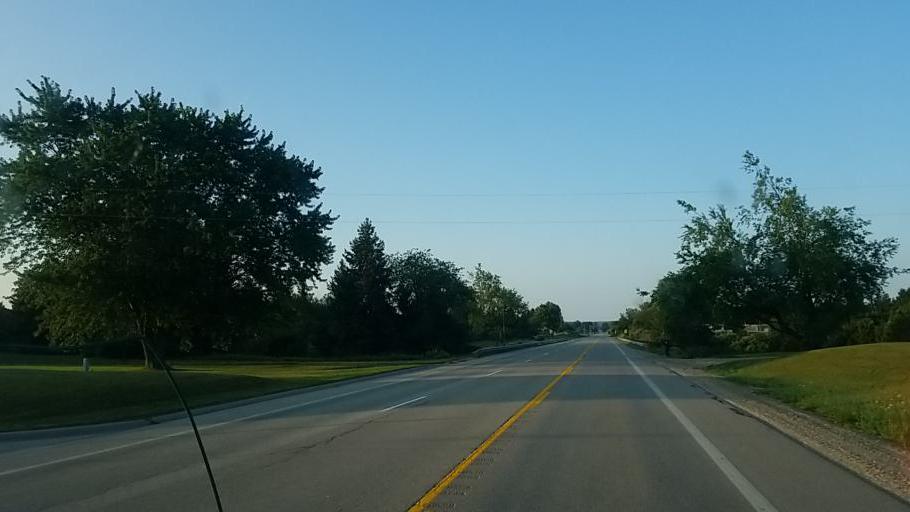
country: US
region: Michigan
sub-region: Isabella County
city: Lake Isabella
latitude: 43.6721
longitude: -85.1464
